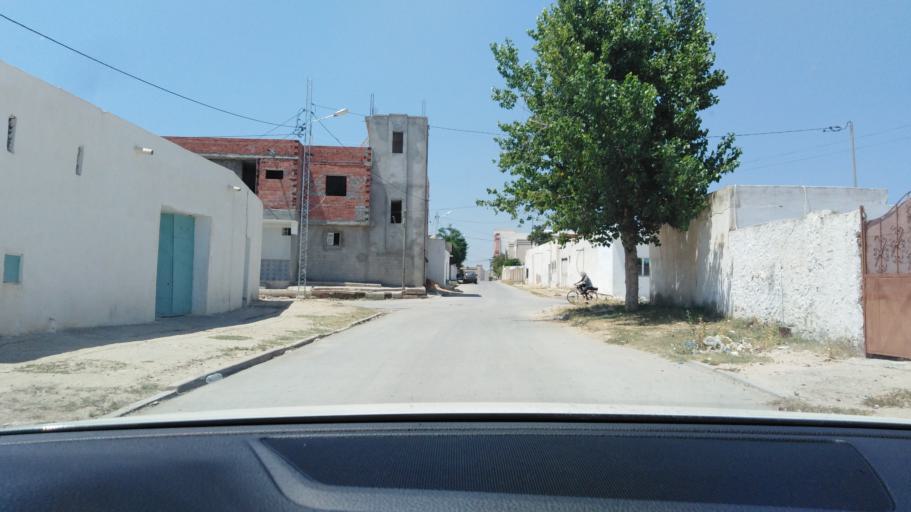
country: TN
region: Al Qayrawan
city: Sbikha
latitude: 36.1147
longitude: 10.0944
